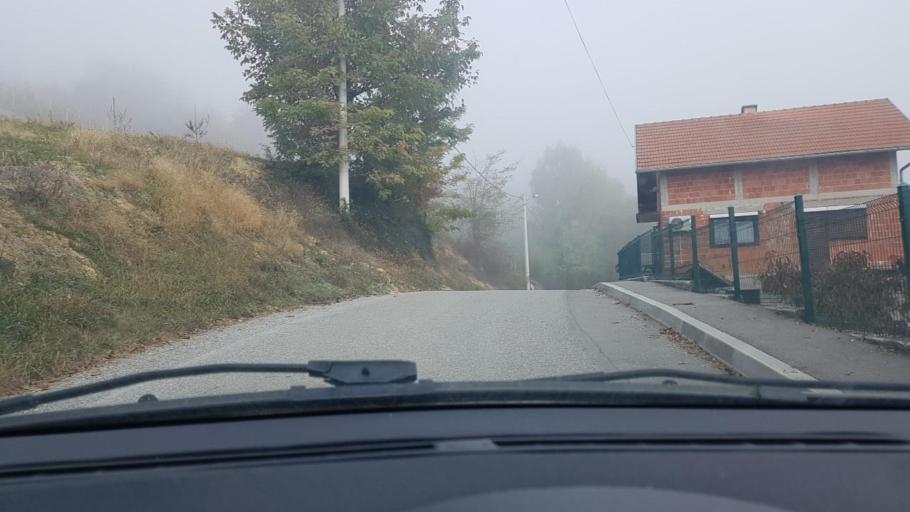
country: HR
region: Krapinsko-Zagorska
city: Mihovljan
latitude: 46.1575
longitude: 15.9896
